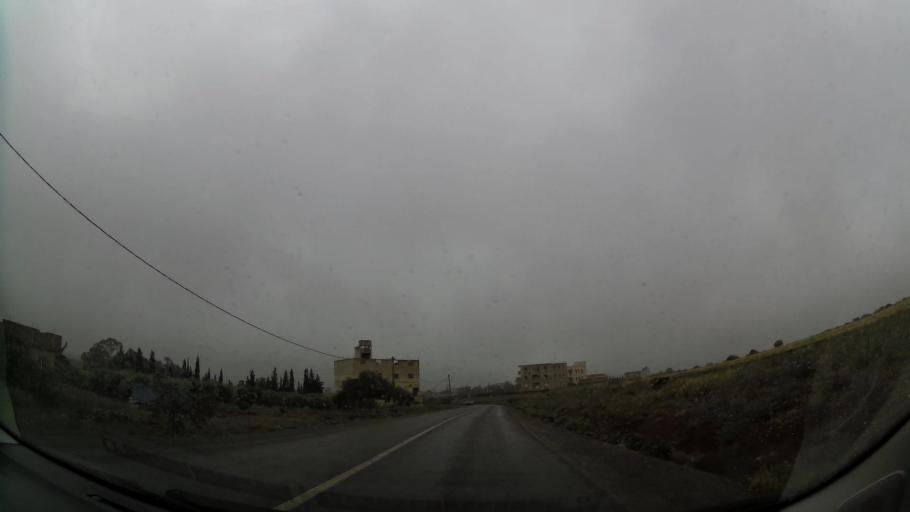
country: MA
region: Oriental
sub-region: Nador
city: Boudinar
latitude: 35.1411
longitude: -3.6139
